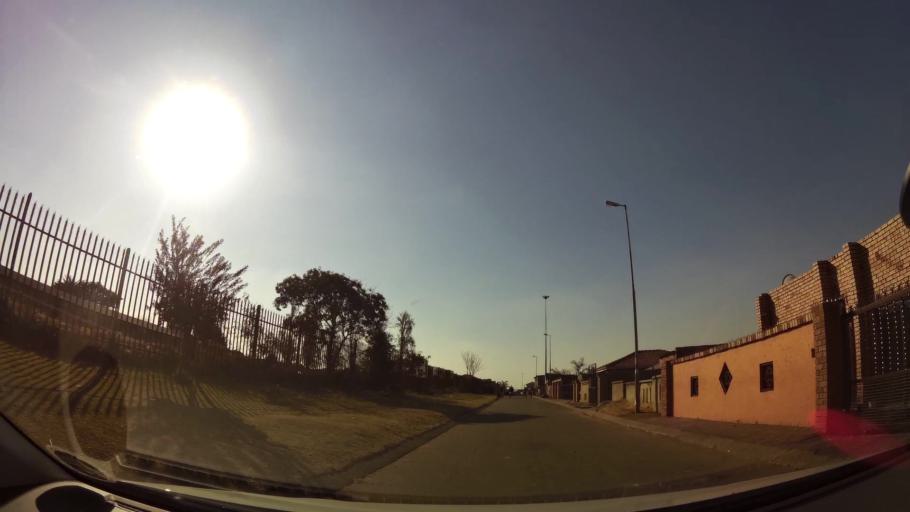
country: ZA
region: Gauteng
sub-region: City of Johannesburg Metropolitan Municipality
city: Soweto
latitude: -26.2763
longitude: 27.8796
